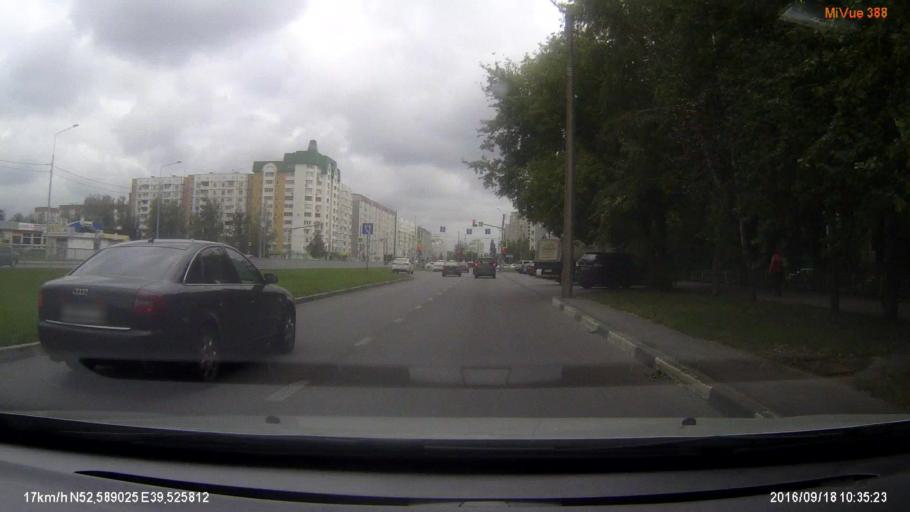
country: RU
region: Lipetsk
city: Syrskoye
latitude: 52.5867
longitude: 39.5306
